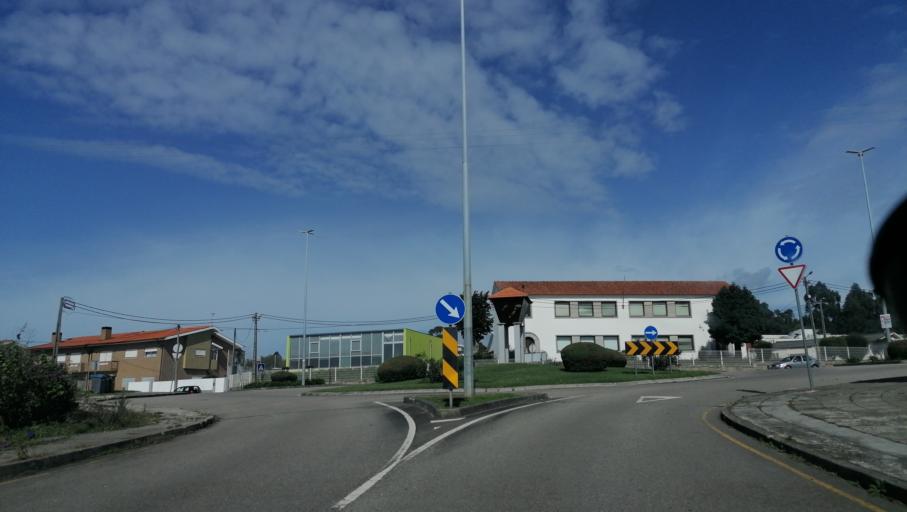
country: PT
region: Aveiro
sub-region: Espinho
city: Silvalde
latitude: 40.9978
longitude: -8.6167
